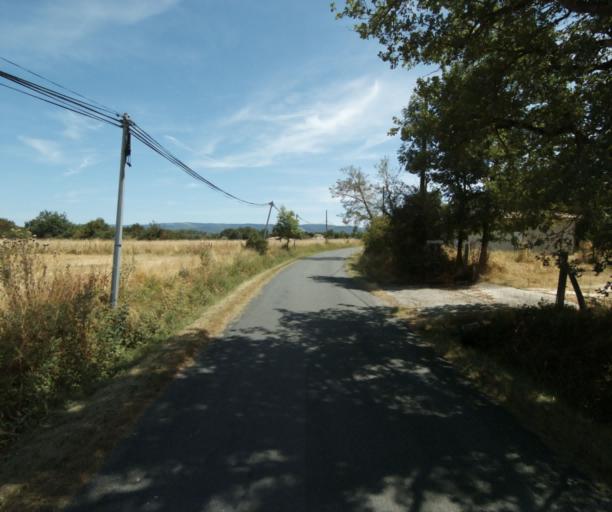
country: FR
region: Midi-Pyrenees
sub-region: Departement de la Haute-Garonne
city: Revel
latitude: 43.5009
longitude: 2.0025
